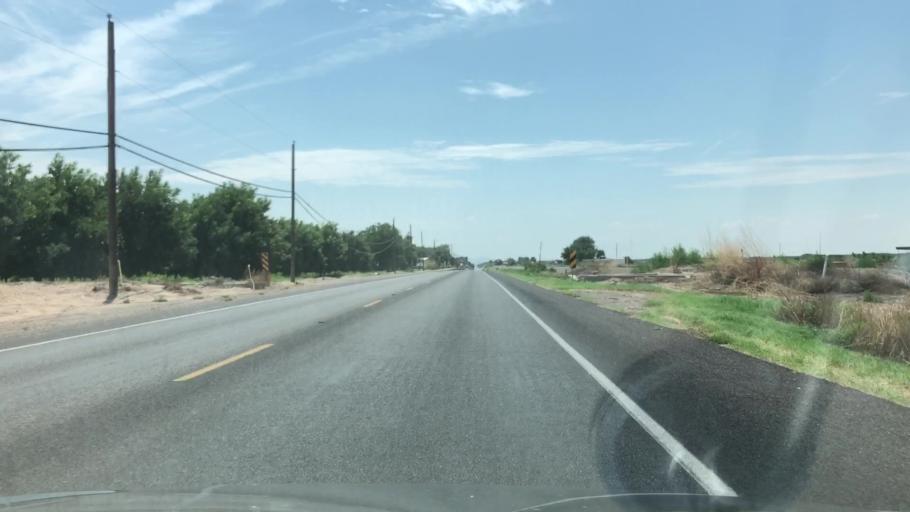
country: US
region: New Mexico
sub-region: Dona Ana County
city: University Park
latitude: 32.2522
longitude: -106.7521
